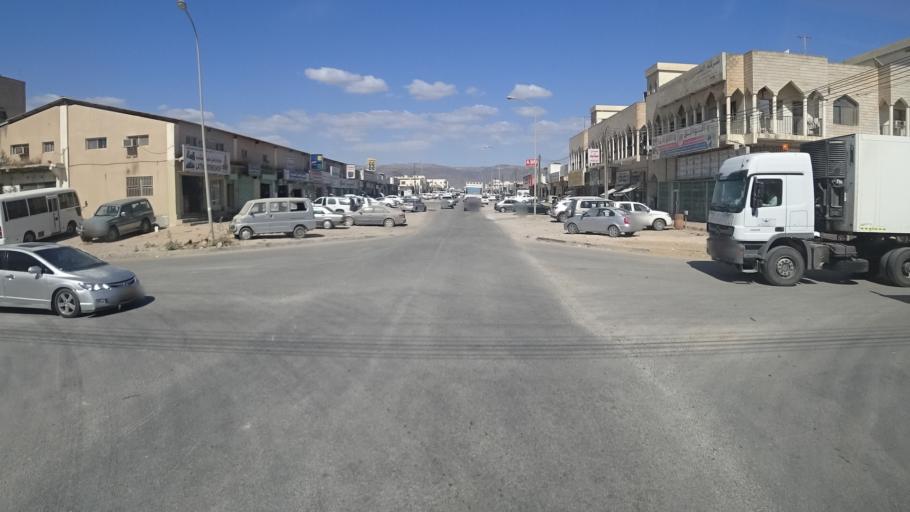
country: OM
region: Zufar
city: Salalah
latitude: 17.0164
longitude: 54.0542
